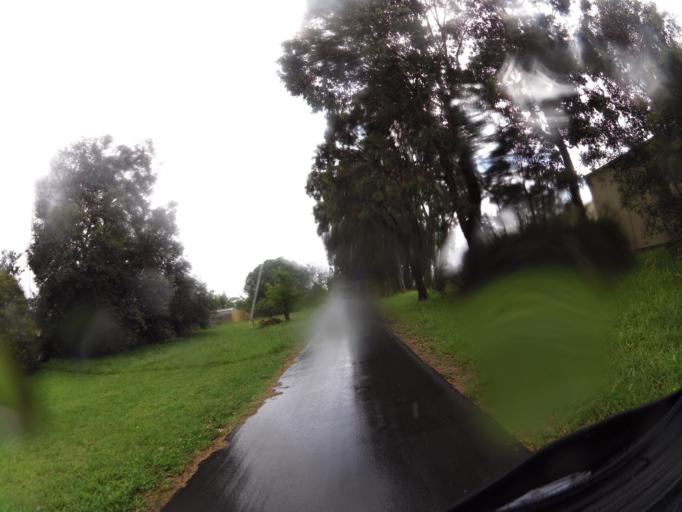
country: AU
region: Victoria
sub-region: East Gippsland
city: Bairnsdale
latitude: -37.8243
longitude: 147.6517
